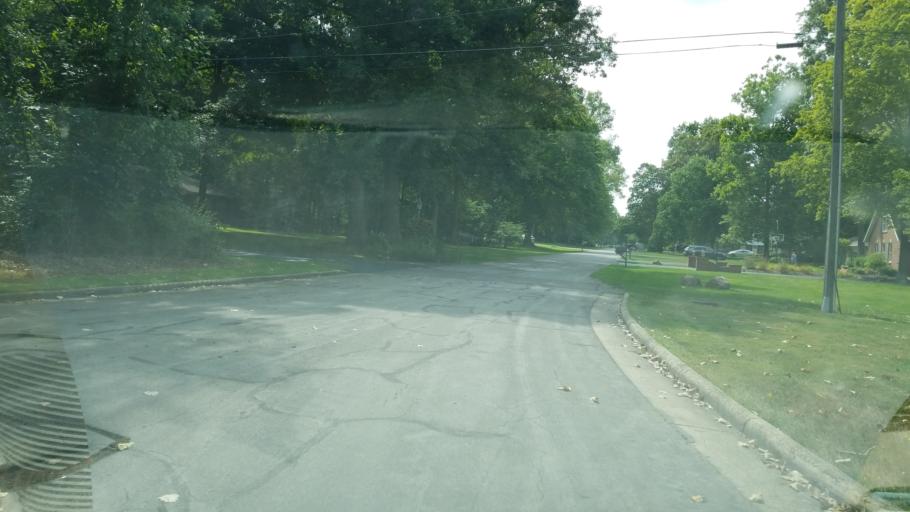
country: US
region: Ohio
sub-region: Marion County
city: Marion
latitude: 40.5324
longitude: -83.0882
